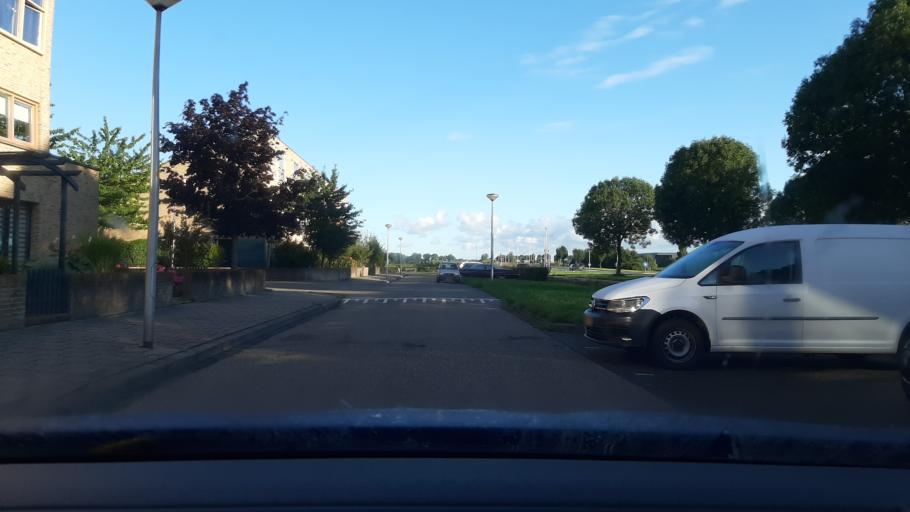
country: NL
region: Flevoland
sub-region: Gemeente Zeewolde
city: Zeewolde
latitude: 52.3439
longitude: 5.5180
